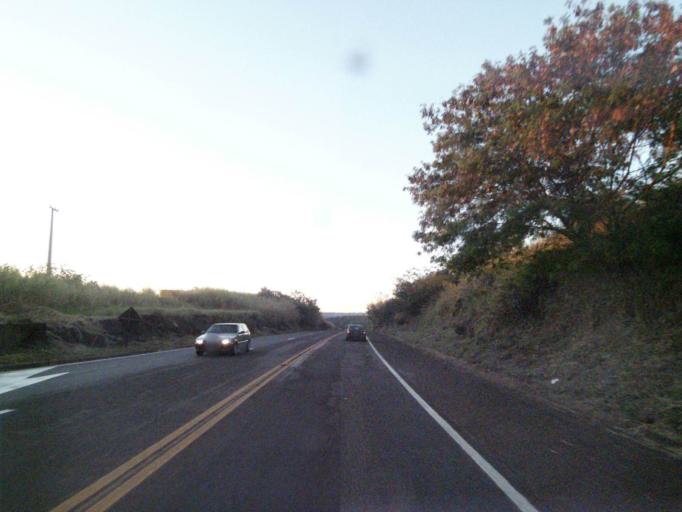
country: BR
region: Parana
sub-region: Londrina
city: Londrina
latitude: -23.4367
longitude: -51.1388
